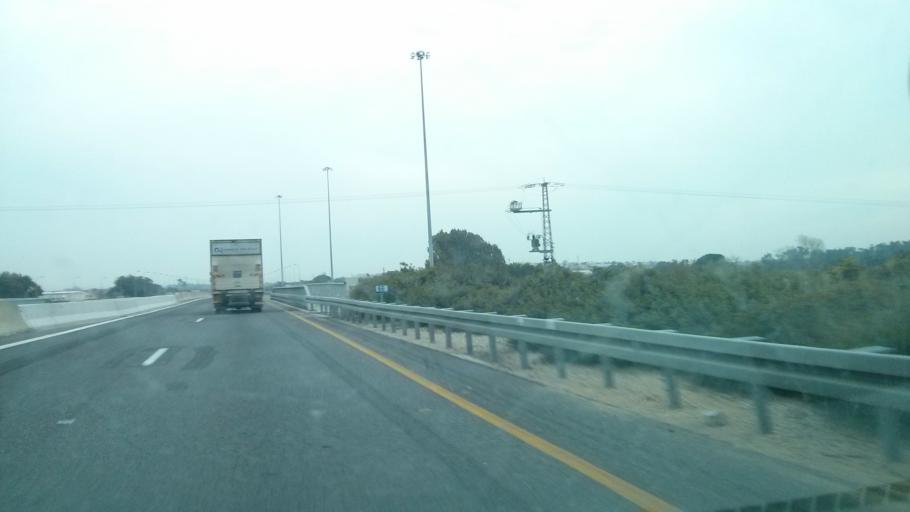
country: IL
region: Haifa
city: Qesarya
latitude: 32.5058
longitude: 34.9141
